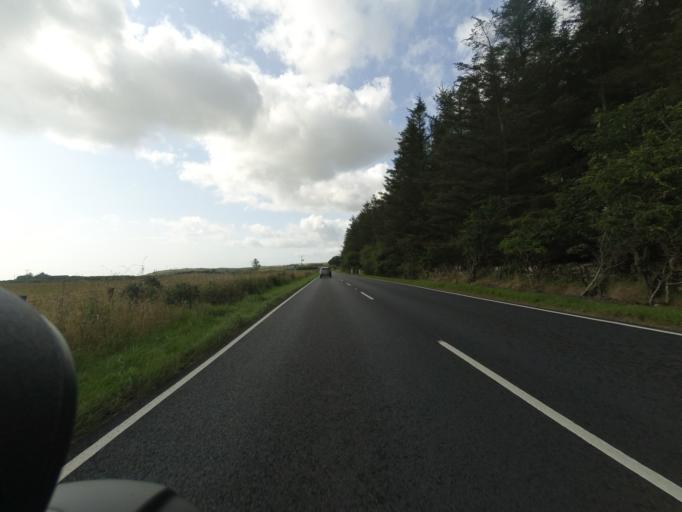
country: GB
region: Scotland
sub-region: Highland
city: Wick
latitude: 58.3866
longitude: -3.1401
